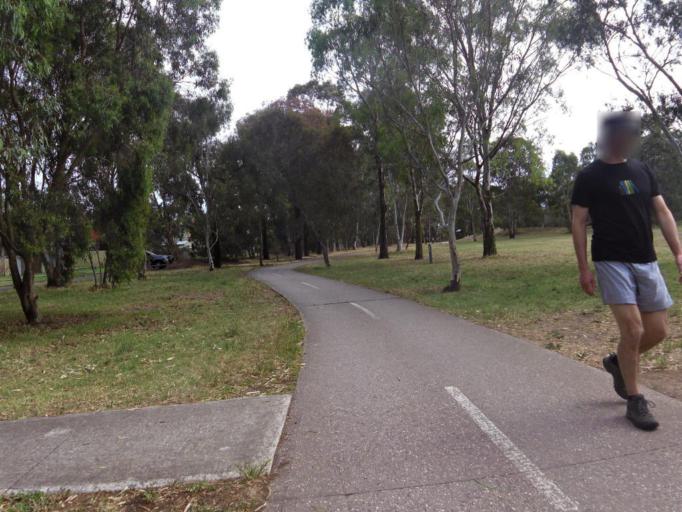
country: AU
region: Victoria
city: Alphington
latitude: -37.7721
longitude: 145.0328
